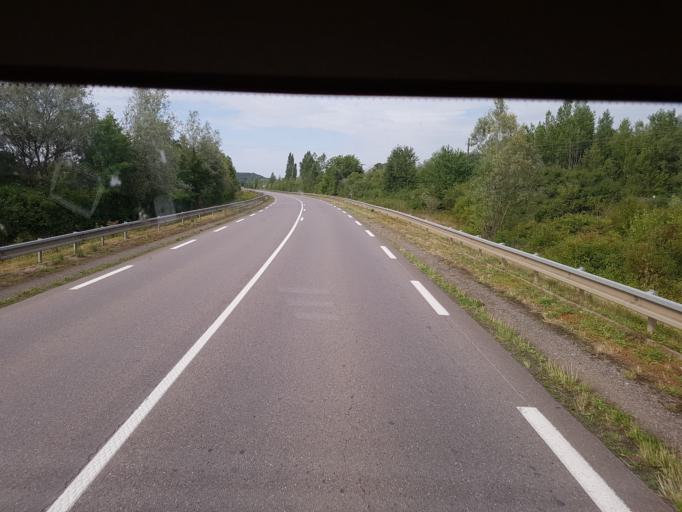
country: FR
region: Lorraine
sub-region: Departement de la Moselle
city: Koenigsmacker
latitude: 49.4046
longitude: 6.2867
